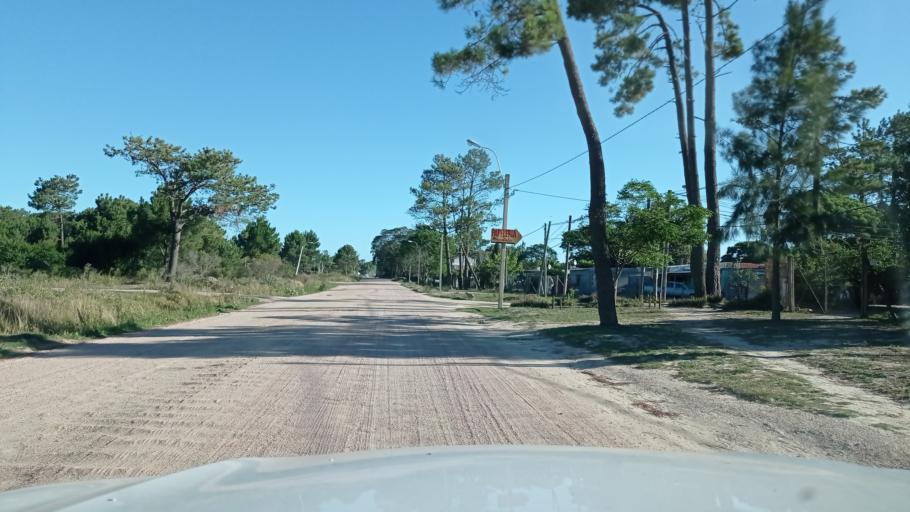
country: UY
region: Canelones
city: Pando
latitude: -34.7911
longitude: -55.9198
